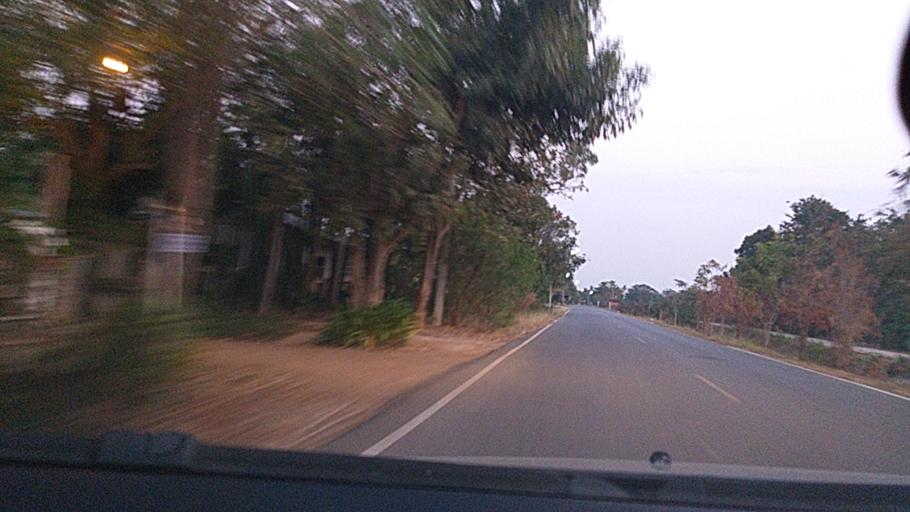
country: TH
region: Sing Buri
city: Sing Buri
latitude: 14.8292
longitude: 100.4039
